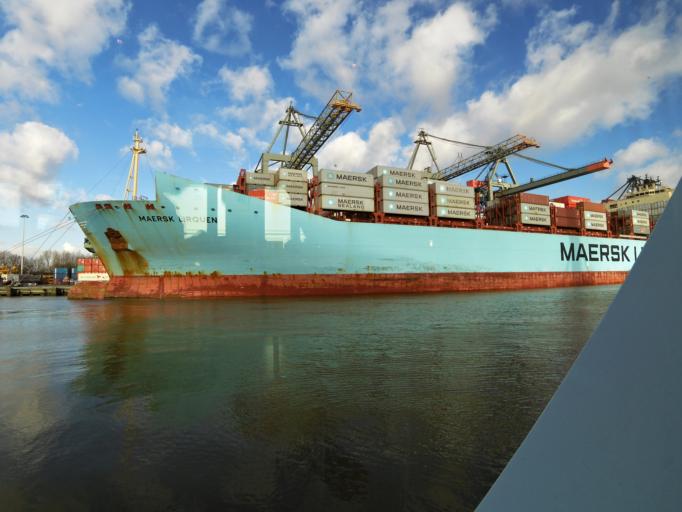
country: NL
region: South Holland
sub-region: Gemeente Rotterdam
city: Delfshaven
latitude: 51.8898
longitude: 4.4291
